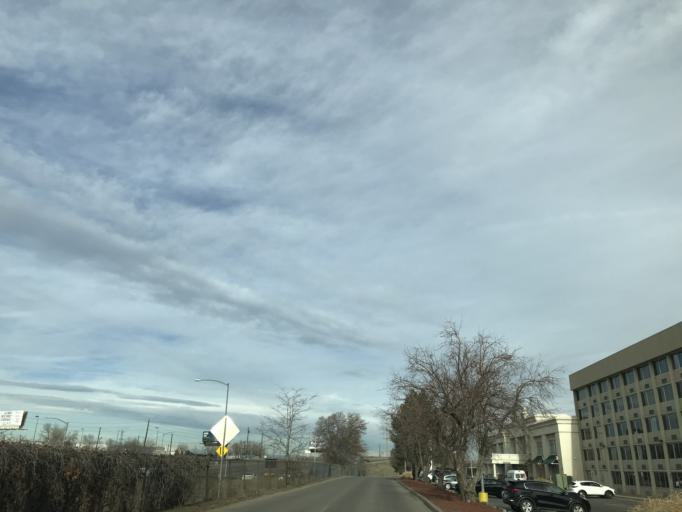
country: US
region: Colorado
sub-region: Adams County
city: Commerce City
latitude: 39.7729
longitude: -104.9021
